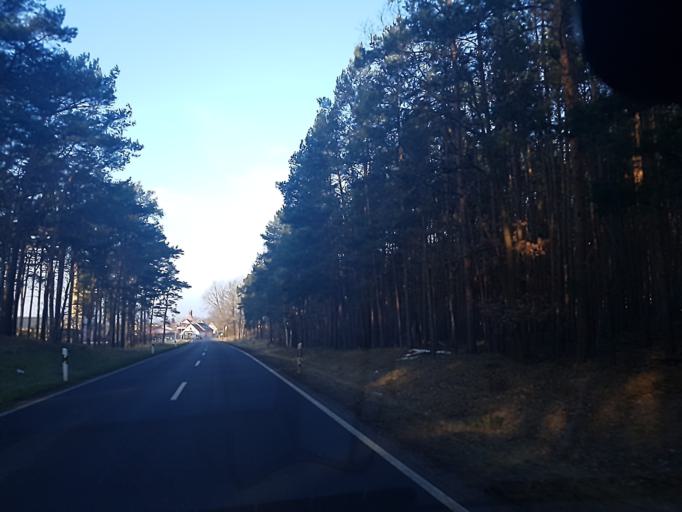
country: DE
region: Brandenburg
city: Golzow
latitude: 52.2784
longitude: 12.6115
